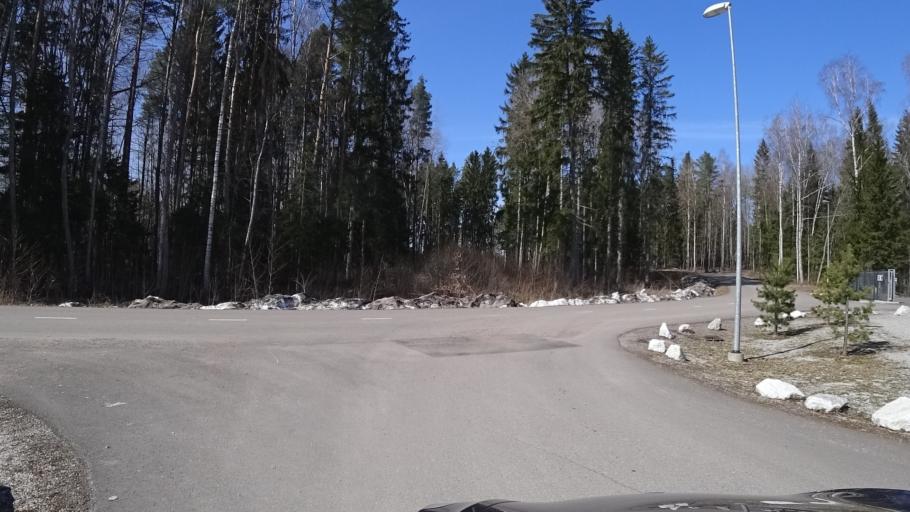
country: FI
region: Uusimaa
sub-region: Helsinki
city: Lohja
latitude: 60.2640
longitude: 24.0678
